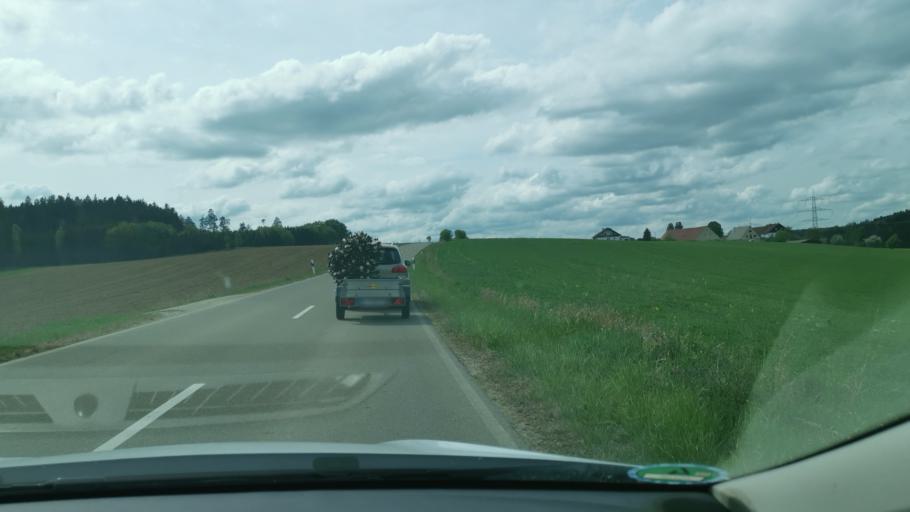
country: DE
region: Bavaria
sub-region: Swabia
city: Affing
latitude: 48.4883
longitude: 10.9689
